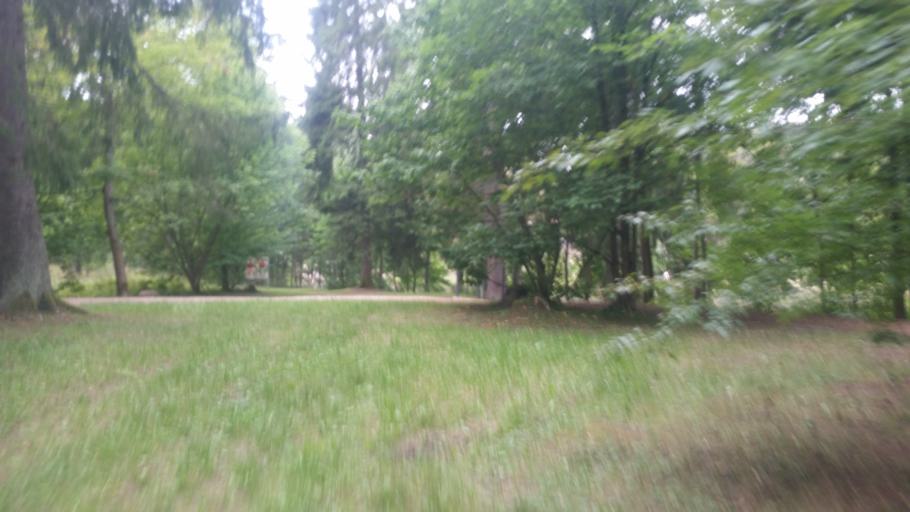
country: LV
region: Ogre
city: Ogre
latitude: 56.8152
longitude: 24.6152
